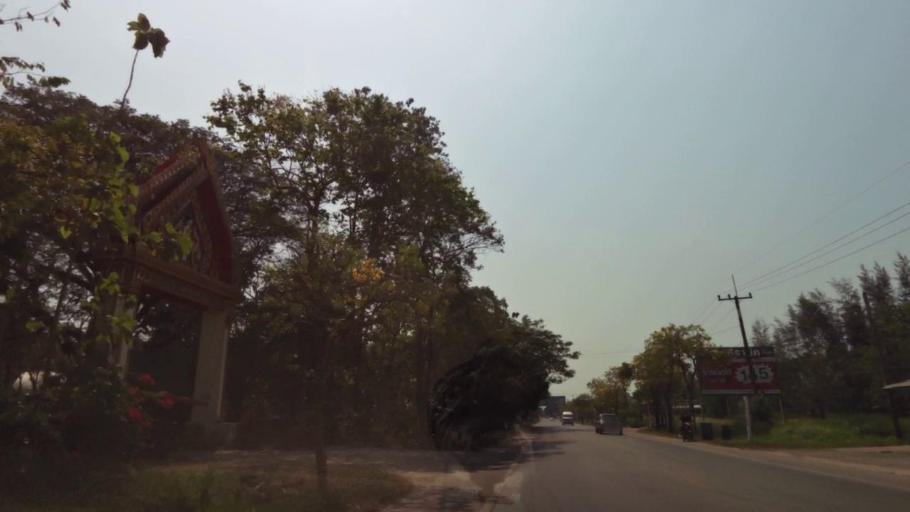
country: TH
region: Chanthaburi
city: Tha Mai
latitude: 12.5667
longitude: 101.9150
